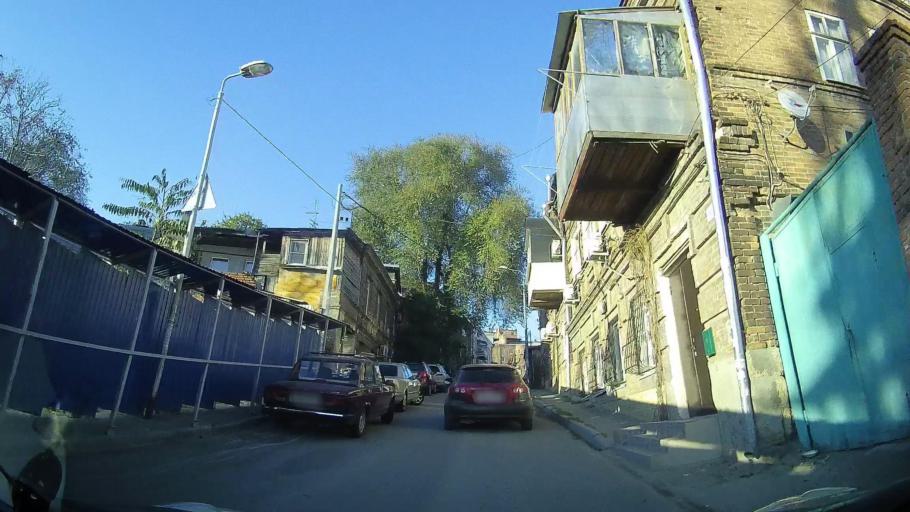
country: RU
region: Rostov
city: Rostov-na-Donu
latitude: 47.2140
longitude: 39.7069
